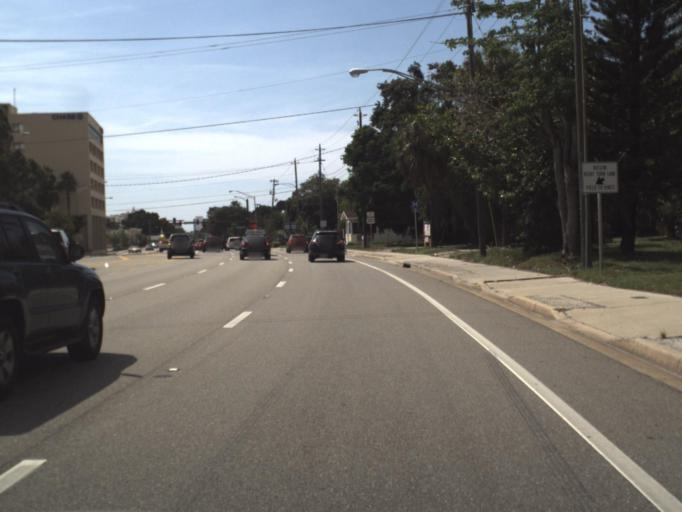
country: US
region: Florida
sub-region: Sarasota County
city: Sarasota
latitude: 27.3389
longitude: -82.5287
